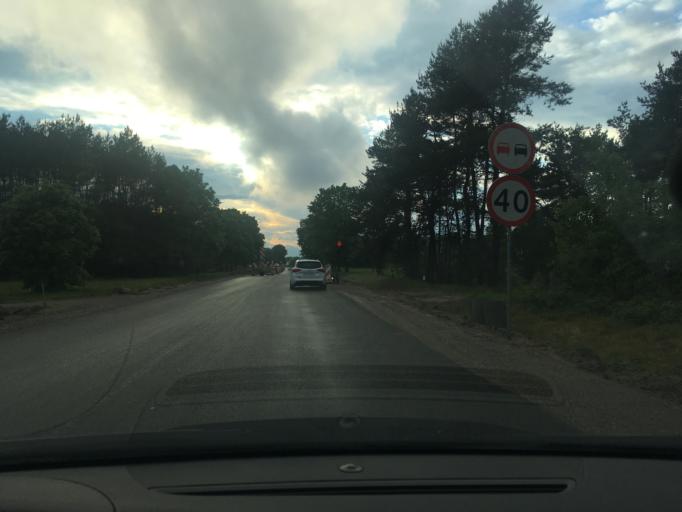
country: PL
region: Lublin Voivodeship
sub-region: Powiat rycki
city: Stezyca
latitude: 51.5966
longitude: 21.7273
